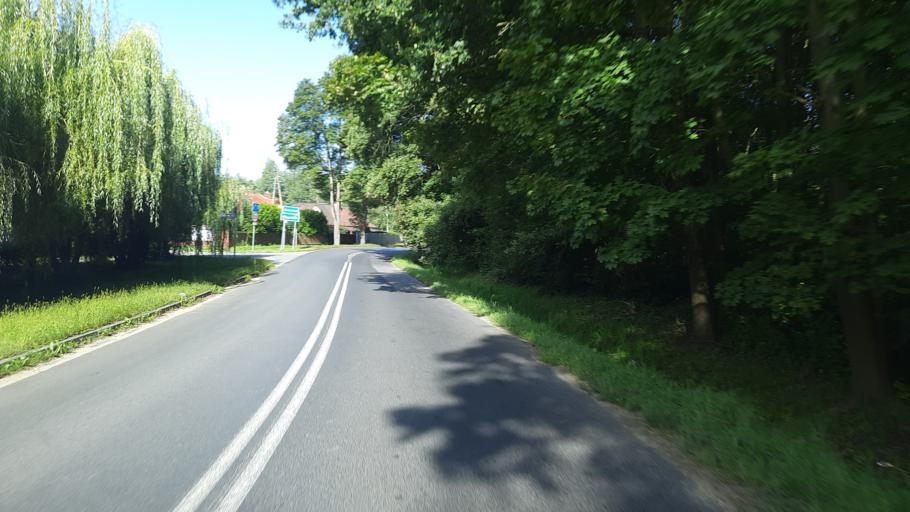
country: PL
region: Lower Silesian Voivodeship
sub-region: Powiat wroclawski
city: Dlugoleka
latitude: 51.1839
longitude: 17.1885
